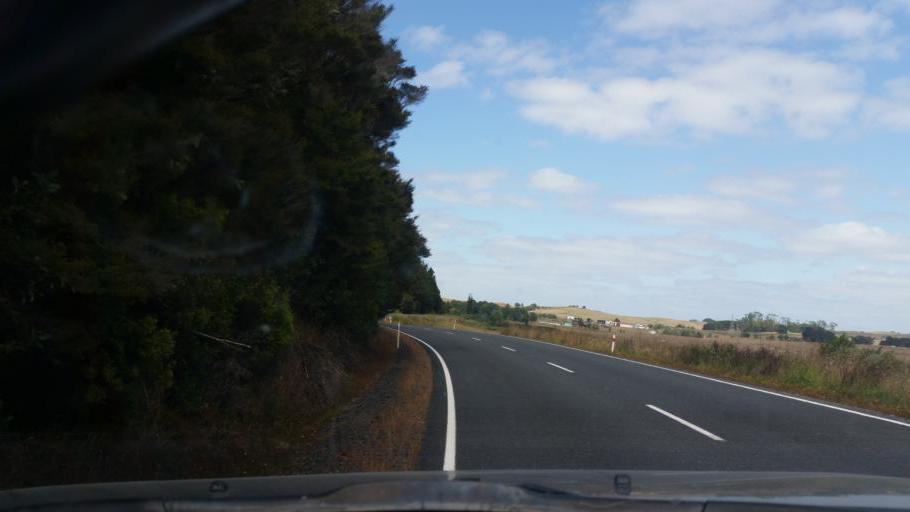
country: NZ
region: Northland
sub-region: Whangarei
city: Ruakaka
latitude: -35.9678
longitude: 174.2905
